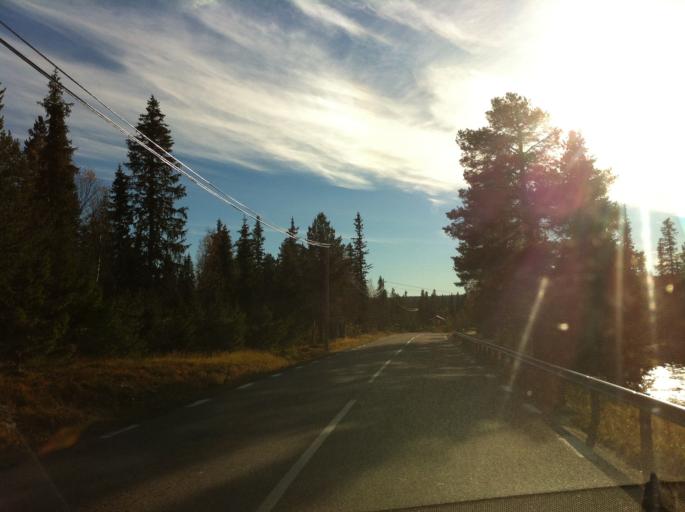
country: NO
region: Hedmark
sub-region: Engerdal
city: Engerdal
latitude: 62.0788
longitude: 12.3093
